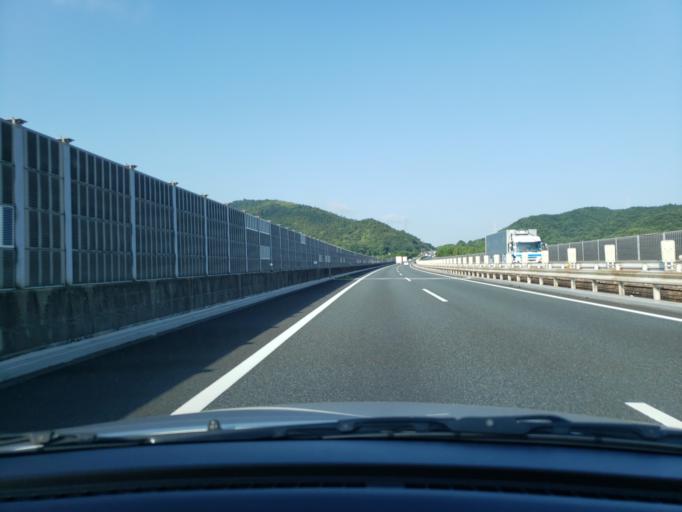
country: JP
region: Okayama
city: Kamogatacho-kamogata
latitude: 34.5375
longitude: 133.5606
